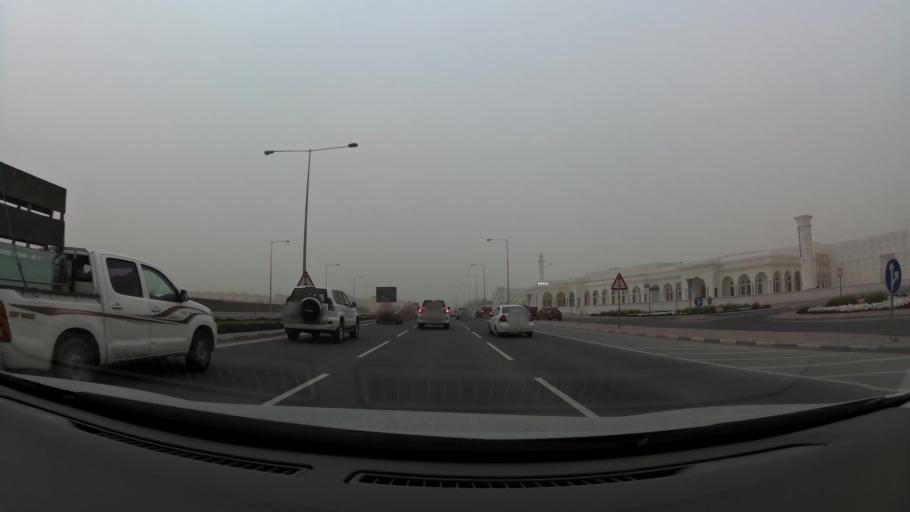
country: QA
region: Baladiyat ad Dawhah
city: Doha
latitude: 25.2429
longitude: 51.4948
